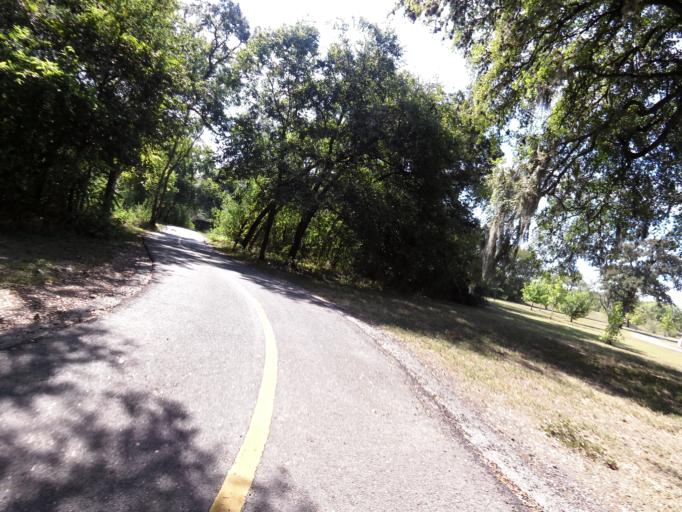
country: US
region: Texas
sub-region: Bexar County
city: Kirby
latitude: 29.4141
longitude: -98.4170
